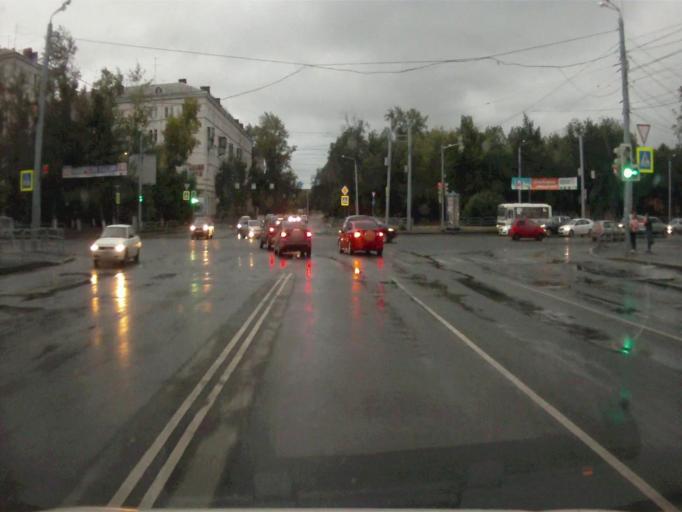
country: RU
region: Chelyabinsk
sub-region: Gorod Chelyabinsk
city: Chelyabinsk
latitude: 55.1616
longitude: 61.4337
